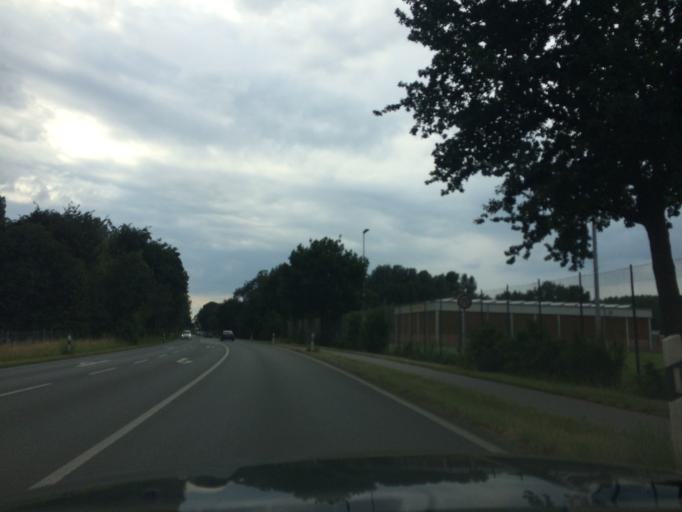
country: DE
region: North Rhine-Westphalia
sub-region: Regierungsbezirk Dusseldorf
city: Weeze
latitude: 51.6313
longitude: 6.2022
